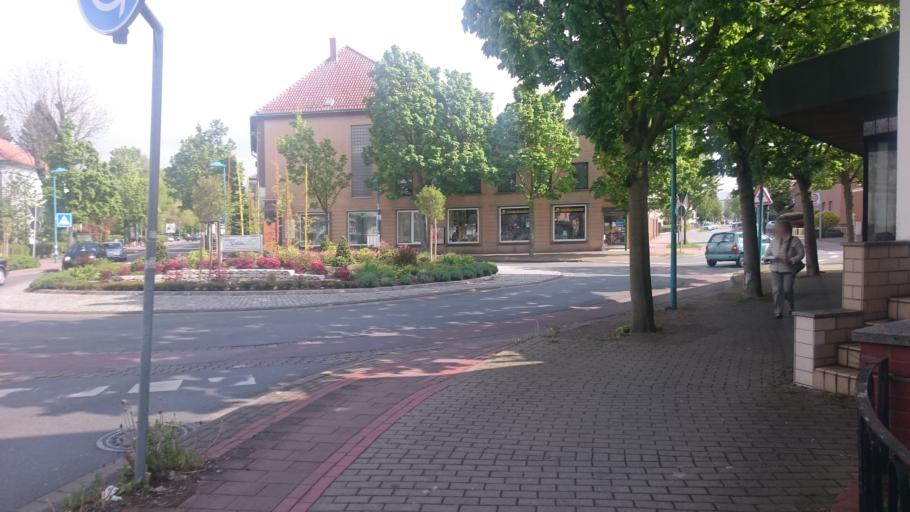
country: DE
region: Lower Saxony
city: Stadthagen
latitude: 52.3278
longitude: 9.1965
